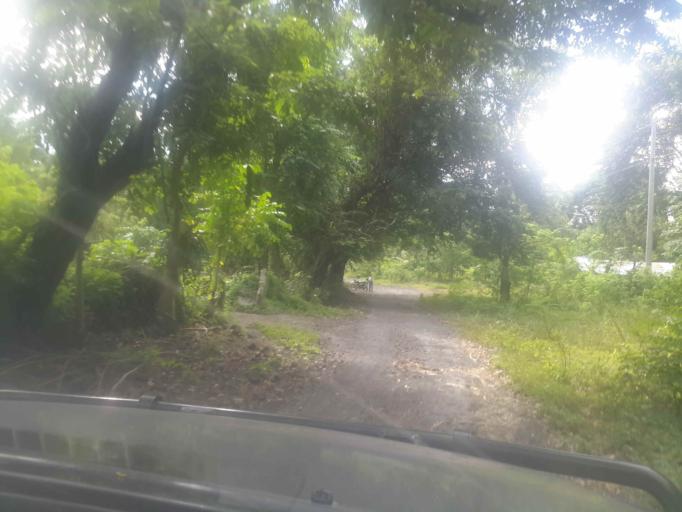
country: NI
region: Rivas
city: Altagracia
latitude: 11.5085
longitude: -85.6041
